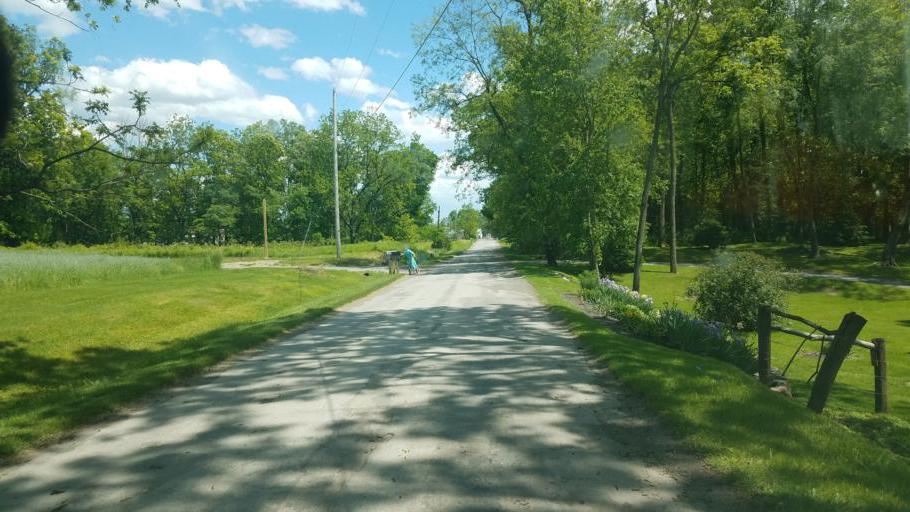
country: US
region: Ohio
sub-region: Geauga County
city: Middlefield
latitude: 41.4187
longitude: -80.9999
